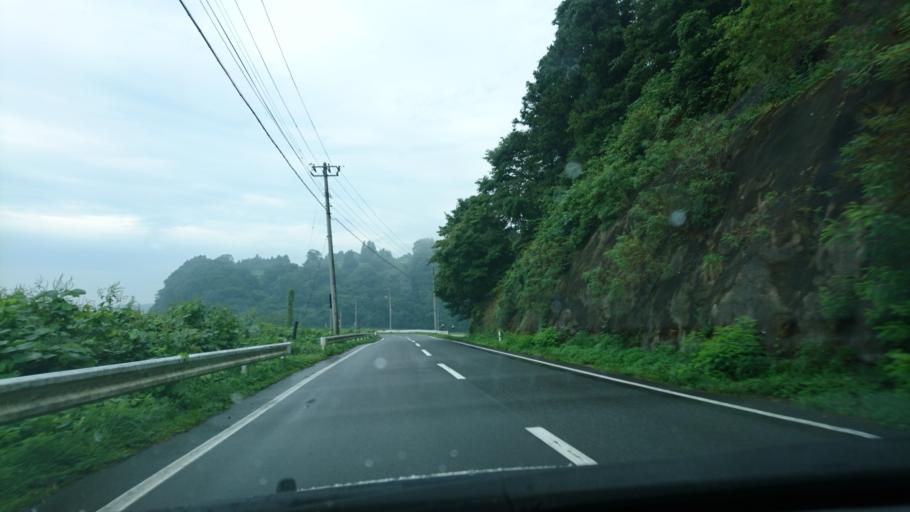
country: JP
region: Iwate
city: Ichinoseki
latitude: 38.8868
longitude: 141.2658
